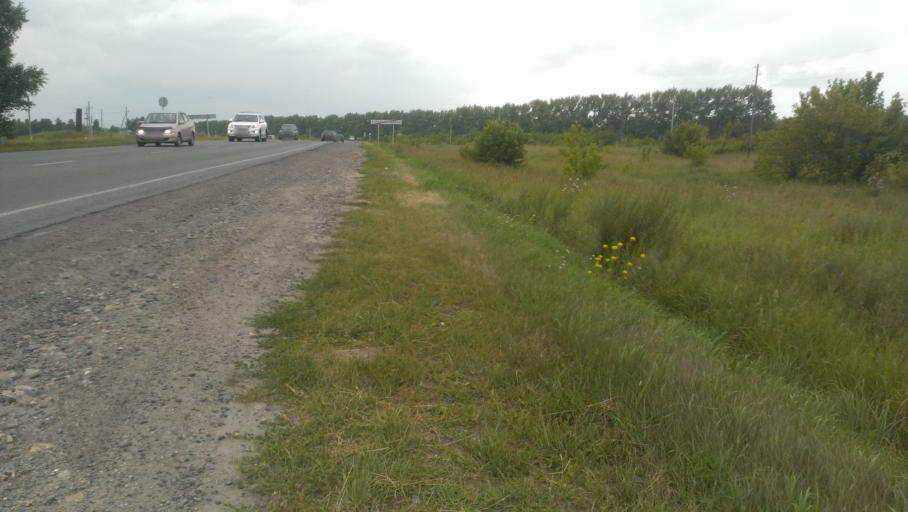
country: RU
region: Altai Krai
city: Gon'ba
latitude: 53.3898
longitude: 83.6011
